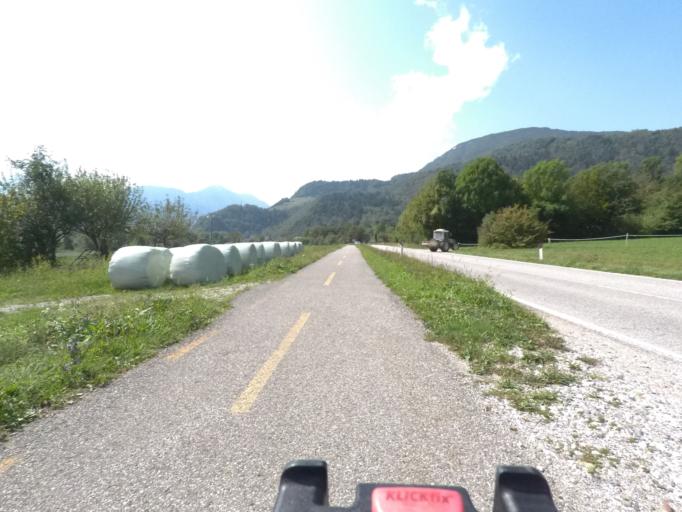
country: IT
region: Friuli Venezia Giulia
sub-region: Provincia di Udine
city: Tolmezzo
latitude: 46.4260
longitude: 13.0139
